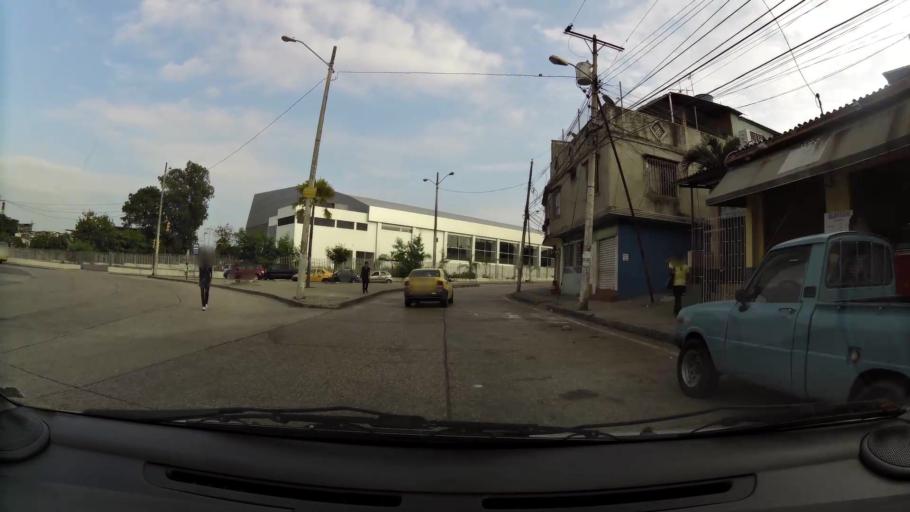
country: EC
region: Guayas
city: Eloy Alfaro
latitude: -2.1325
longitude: -79.8897
